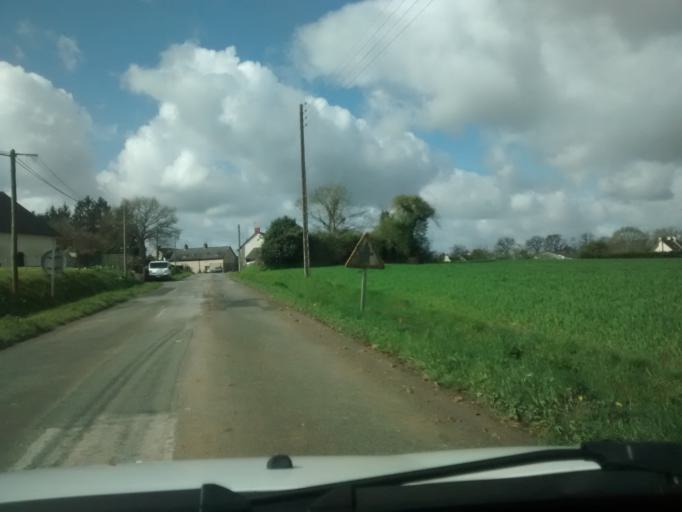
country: FR
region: Brittany
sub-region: Departement d'Ille-et-Vilaine
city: Acigne
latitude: 48.1467
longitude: -1.5241
